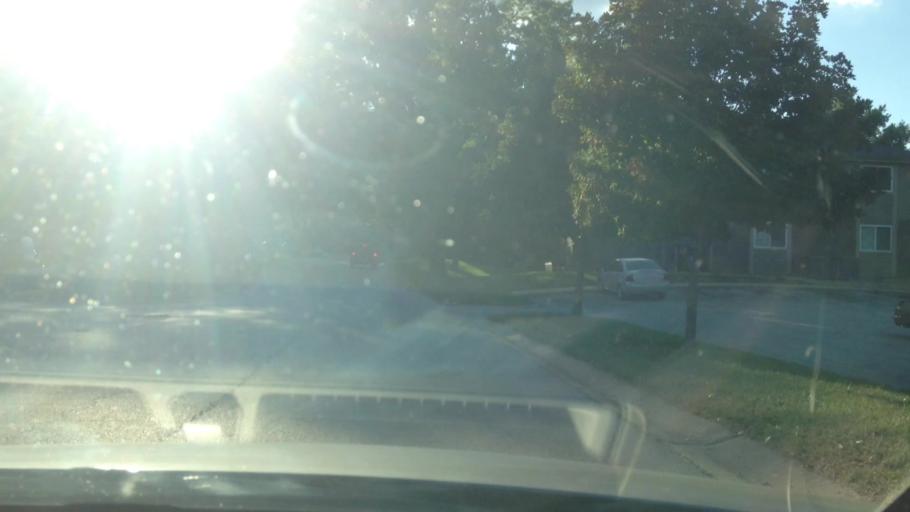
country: US
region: Kansas
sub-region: Johnson County
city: Merriam
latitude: 38.9961
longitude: -94.7038
